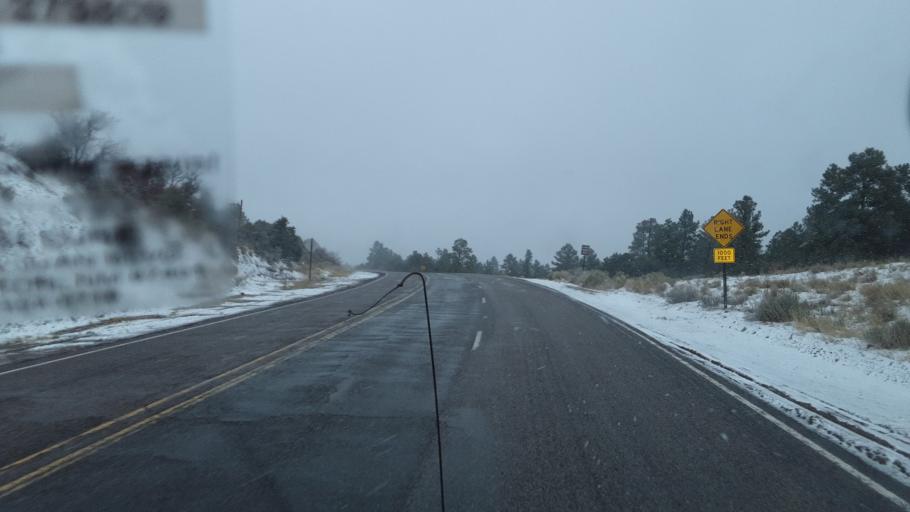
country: US
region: New Mexico
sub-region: Rio Arriba County
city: Tierra Amarilla
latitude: 36.6656
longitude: -106.5570
